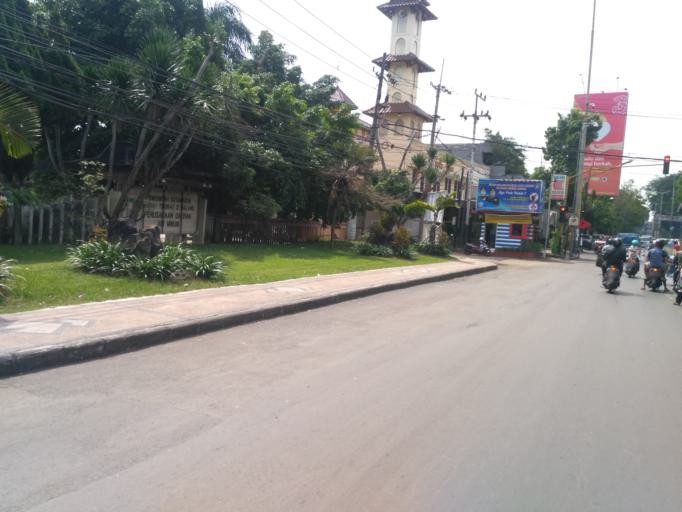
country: ID
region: East Java
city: Malang
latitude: -7.9411
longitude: 112.6425
